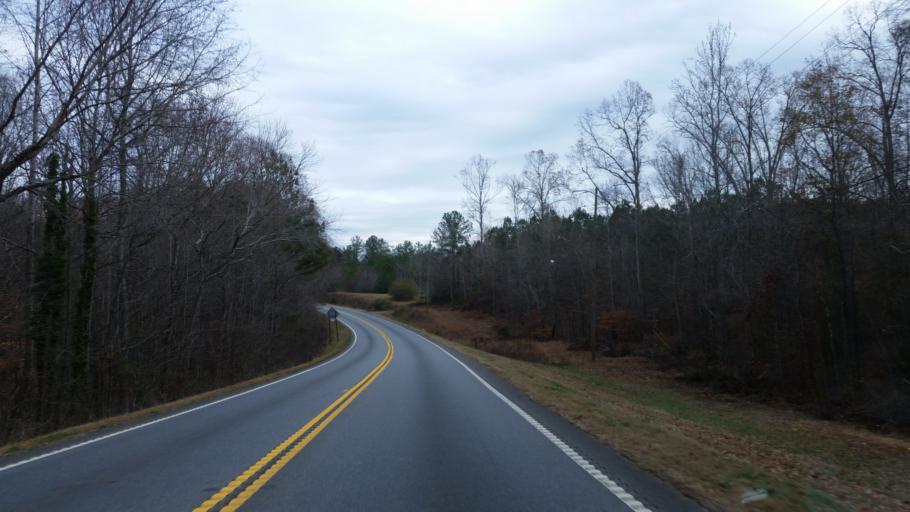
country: US
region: Georgia
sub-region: Cherokee County
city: Holly Springs
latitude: 34.2182
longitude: -84.6097
